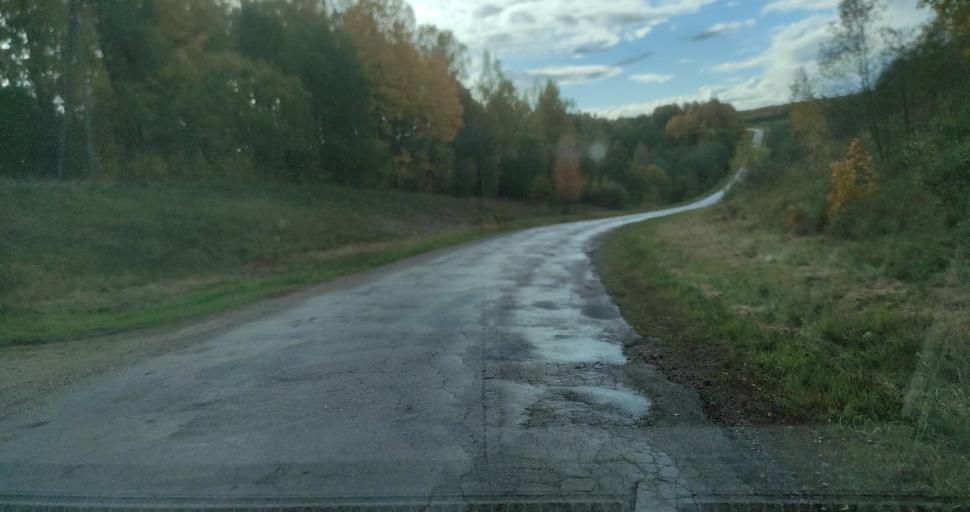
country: LV
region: Vainode
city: Vainode
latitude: 56.5657
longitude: 21.9072
